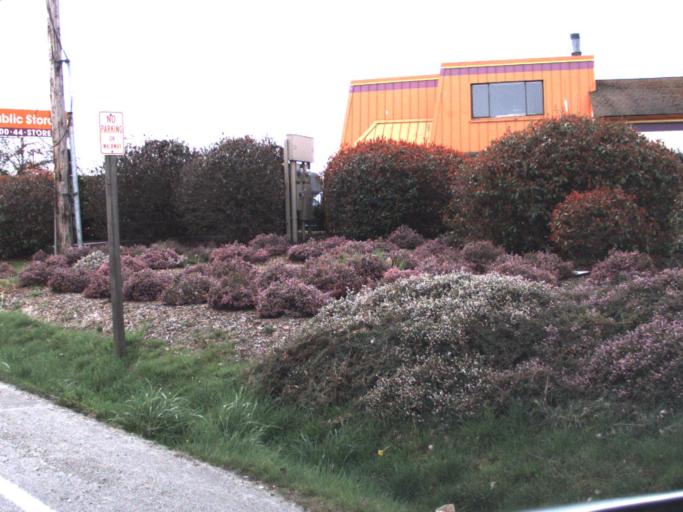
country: US
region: Washington
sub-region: King County
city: Normandy Park
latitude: 47.4410
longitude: -122.3262
